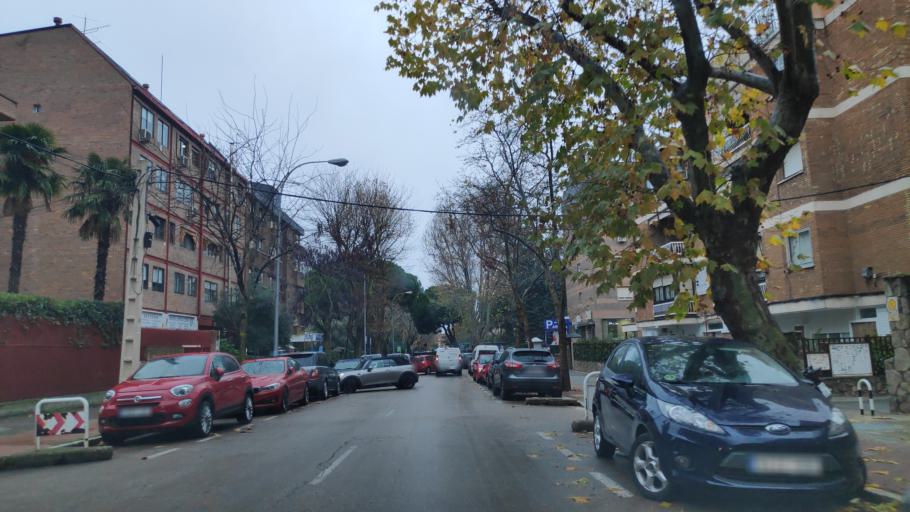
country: ES
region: Madrid
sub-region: Provincia de Madrid
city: Ciudad Lineal
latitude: 40.4541
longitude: -3.6532
